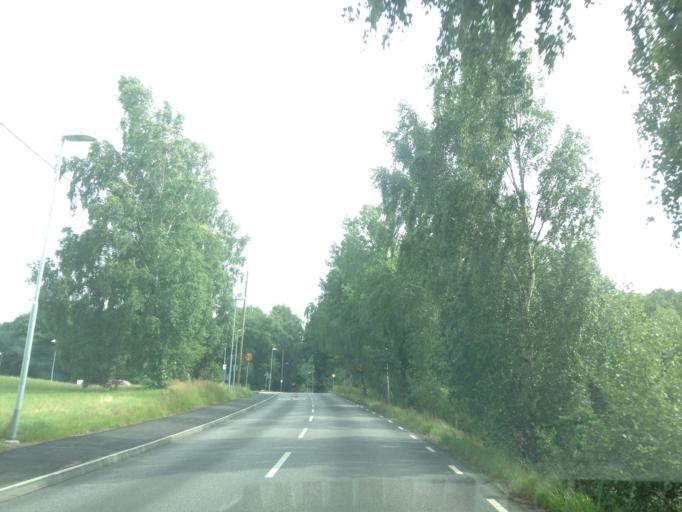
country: SE
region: Vaestra Goetaland
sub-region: Goteborg
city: Goeteborg
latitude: 57.7662
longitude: 11.9494
